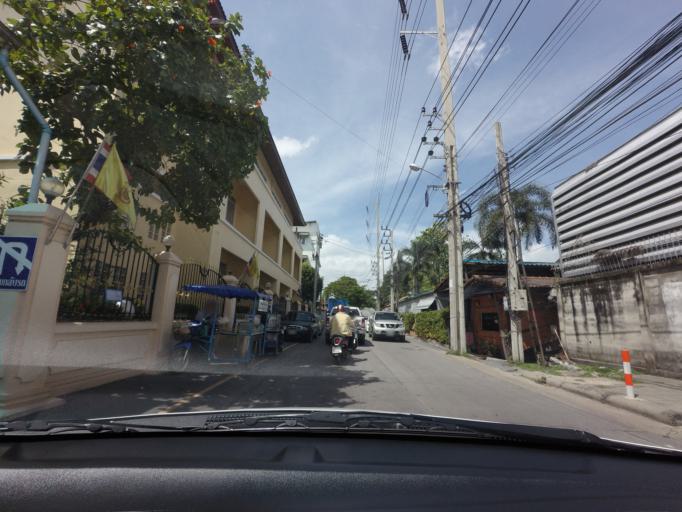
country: TH
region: Bangkok
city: Bang Na
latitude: 13.6126
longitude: 100.6732
